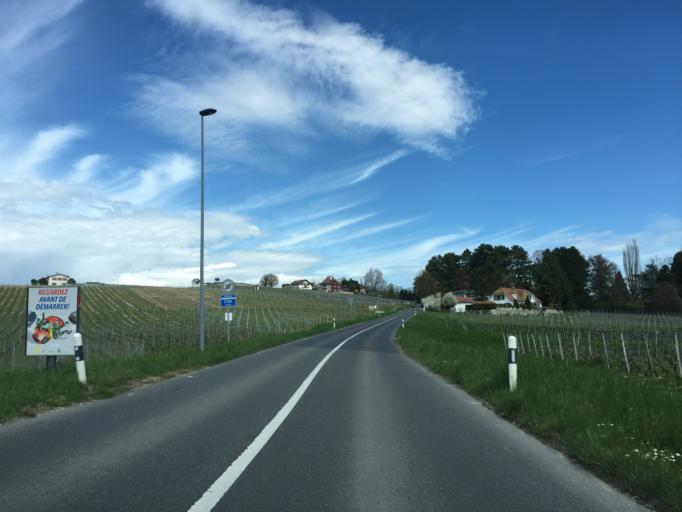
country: CH
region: Vaud
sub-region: Morges District
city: Morges
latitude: 46.5187
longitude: 6.4887
